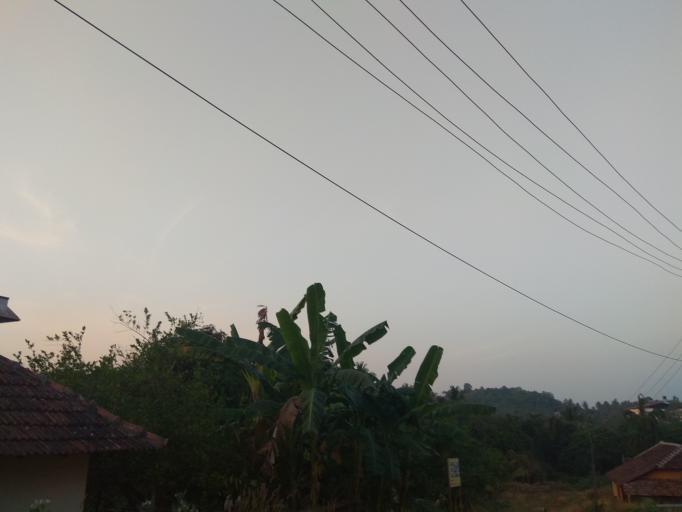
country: IN
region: Karnataka
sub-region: Dakshina Kannada
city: Mangalore
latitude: 12.8935
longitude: 74.8525
